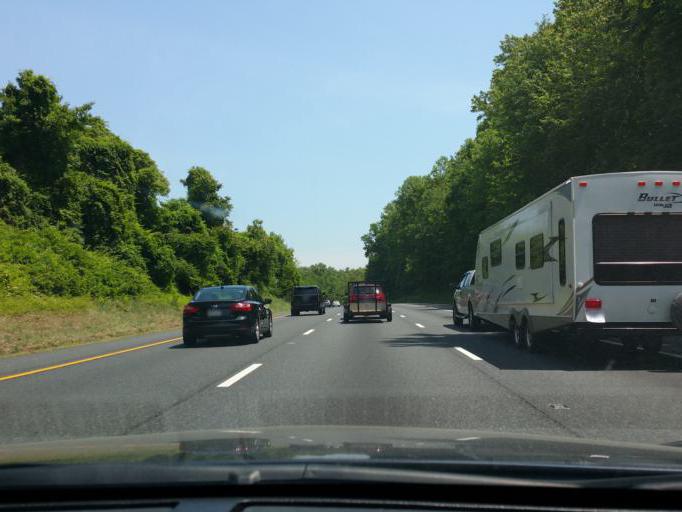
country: US
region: Maryland
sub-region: Harford County
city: Riverside
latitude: 39.4960
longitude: -76.2318
